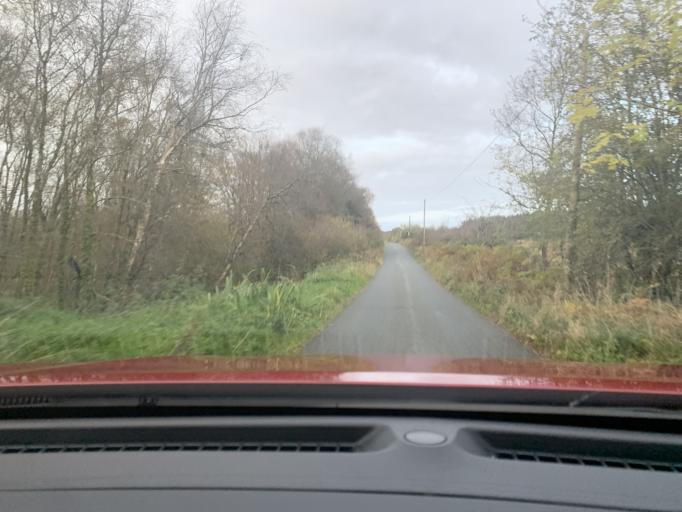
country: IE
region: Connaught
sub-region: Sligo
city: Tobercurry
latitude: 54.0651
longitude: -8.6825
